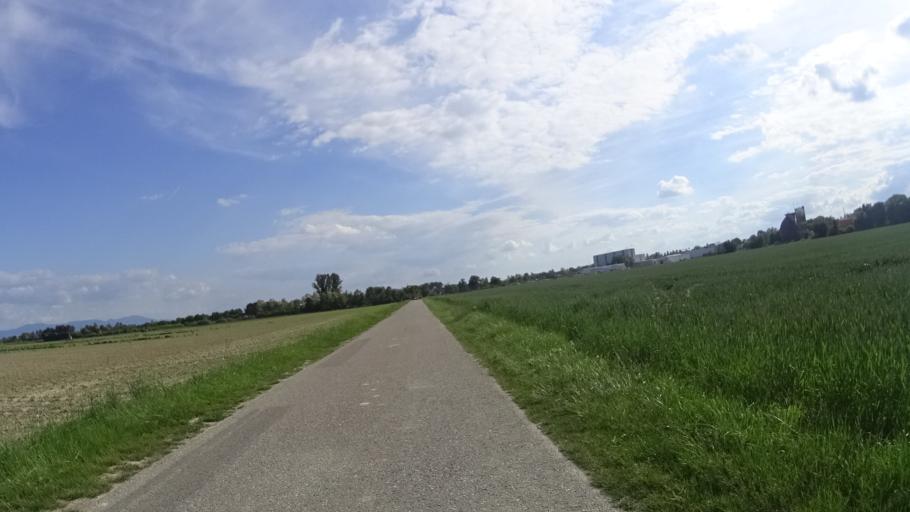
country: DE
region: Baden-Wuerttemberg
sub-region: Freiburg Region
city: Breisach am Rhein
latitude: 48.0510
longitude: 7.5854
